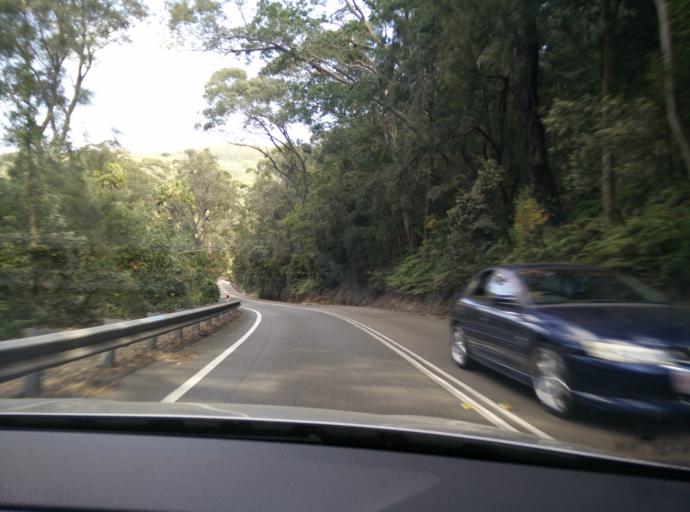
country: AU
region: New South Wales
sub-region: Gosford Shire
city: Blackwall
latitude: -33.4948
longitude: 151.2975
